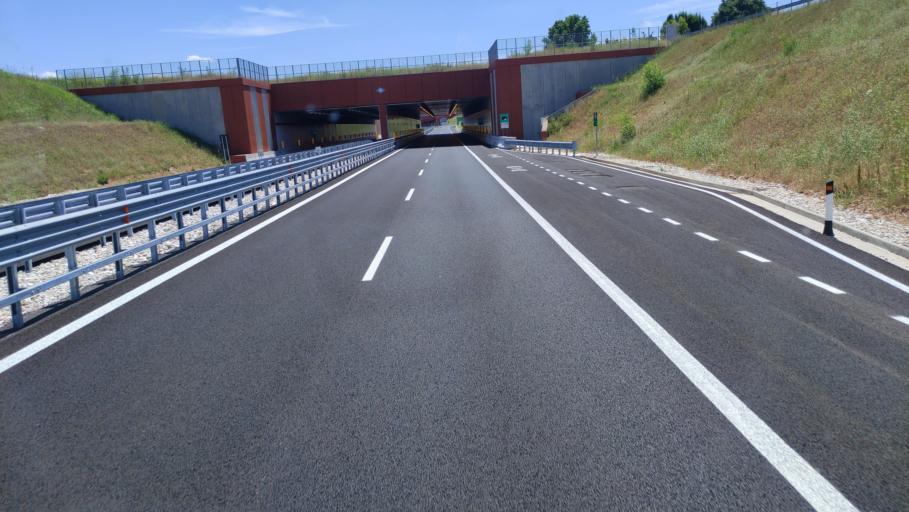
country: IT
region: Veneto
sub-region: Provincia di Treviso
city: Altivole
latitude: 45.7373
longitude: 11.9501
